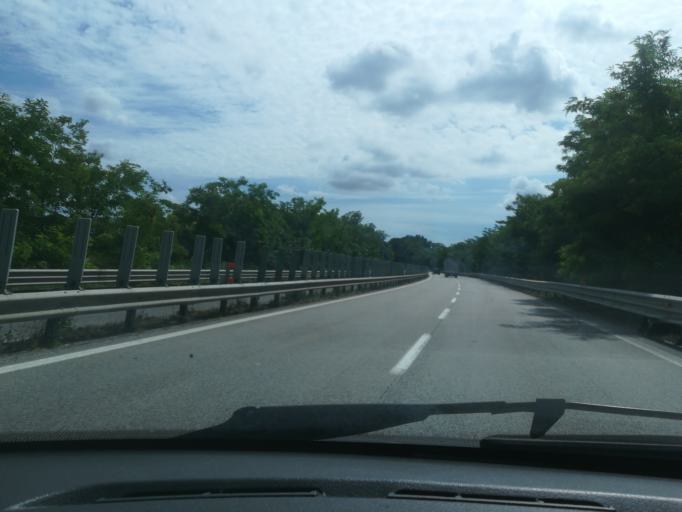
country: IT
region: The Marches
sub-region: Provincia di Macerata
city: Corridonia
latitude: 43.2643
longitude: 13.5332
